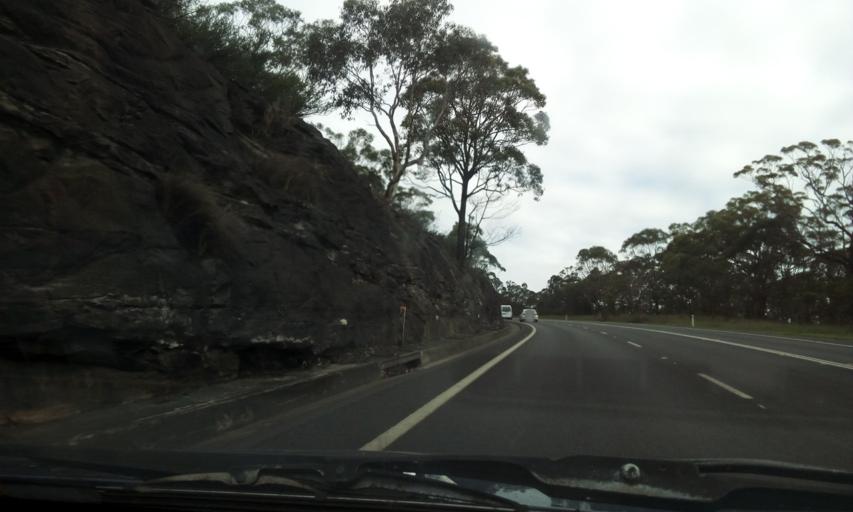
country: AU
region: New South Wales
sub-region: Wollondilly
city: Douglas Park
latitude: -34.2129
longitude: 150.7994
